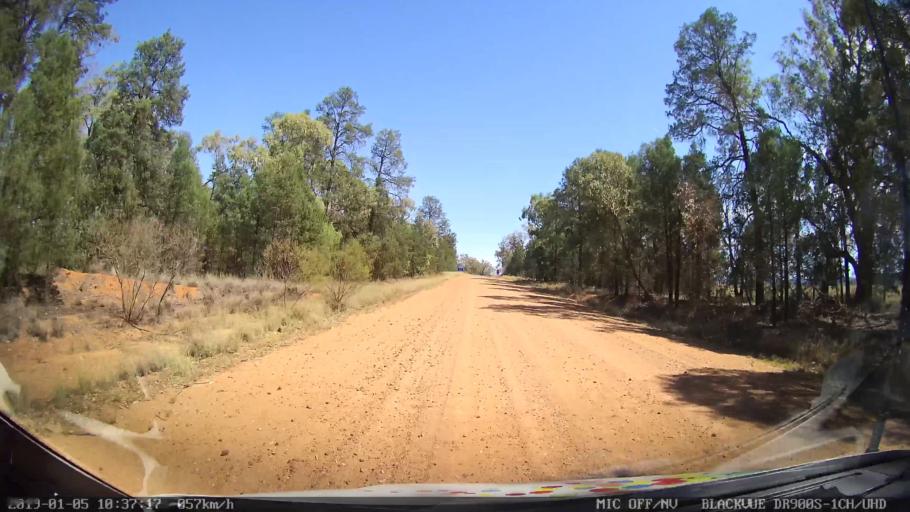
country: AU
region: New South Wales
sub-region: Gilgandra
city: Gilgandra
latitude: -31.4758
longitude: 148.9221
